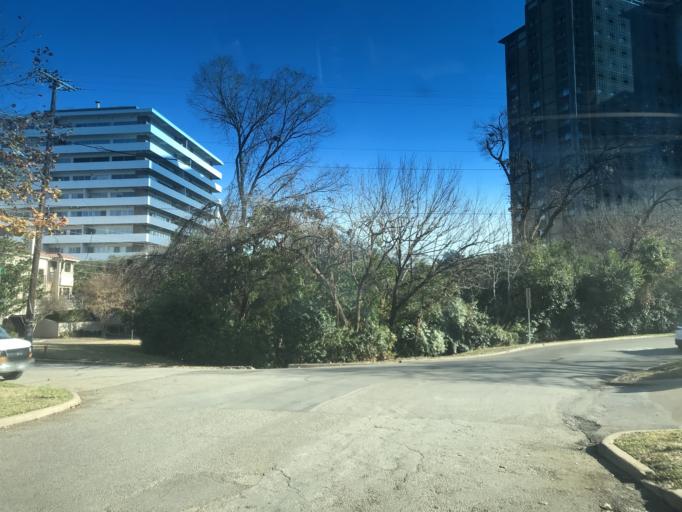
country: US
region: Texas
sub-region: Dallas County
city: Highland Park
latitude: 32.8122
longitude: -96.8037
